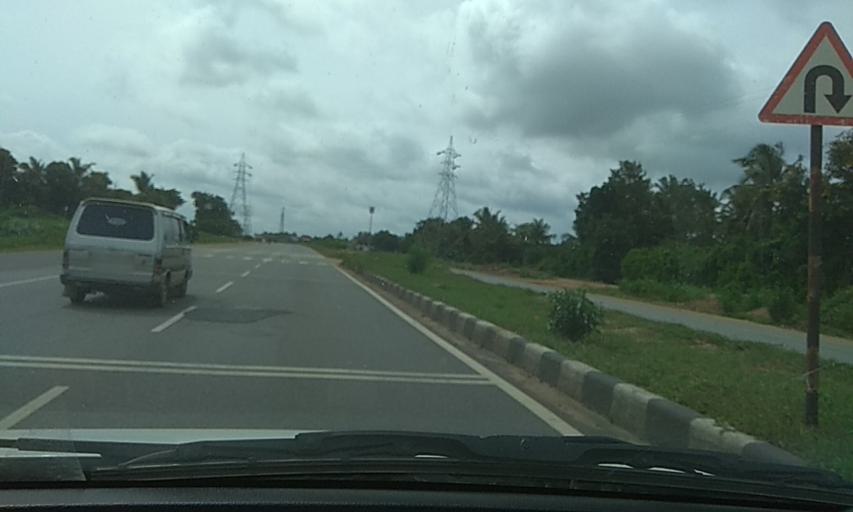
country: IN
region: Karnataka
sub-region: Davanagere
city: Mayakonda
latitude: 14.4158
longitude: 75.9841
